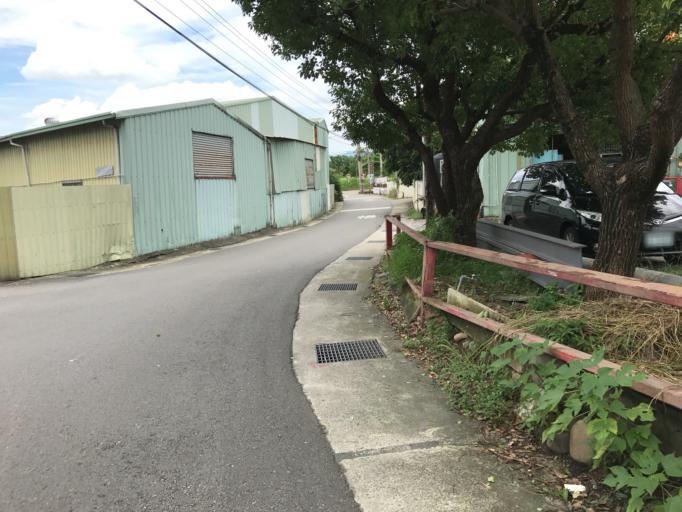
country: TW
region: Taiwan
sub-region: Taichung City
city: Taichung
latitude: 24.0795
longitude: 120.7132
